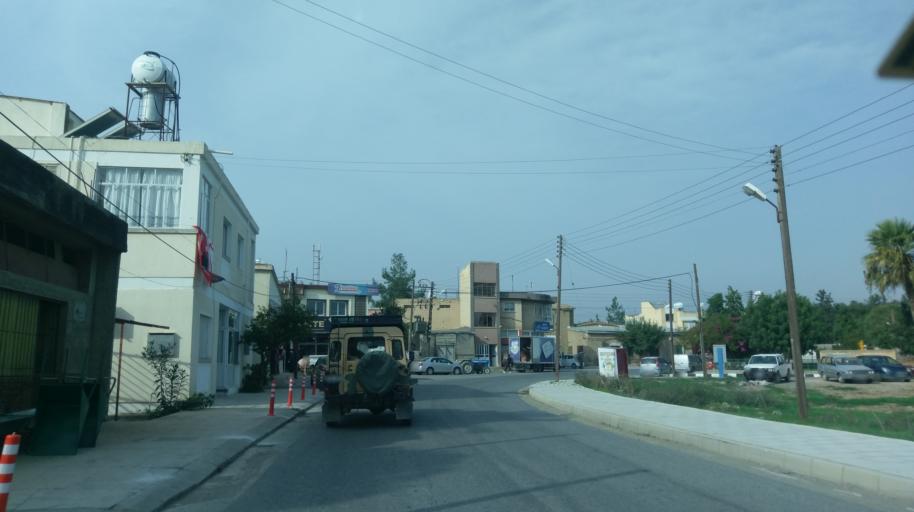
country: CY
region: Lefkosia
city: Mammari
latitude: 35.2311
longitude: 33.1657
